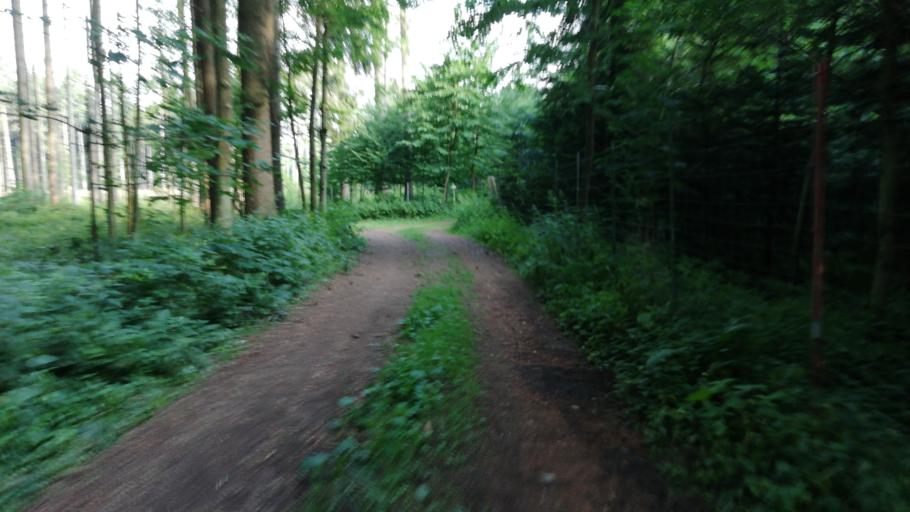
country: AT
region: Upper Austria
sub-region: Wels-Land
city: Buchkirchen
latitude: 48.1890
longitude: 13.9838
